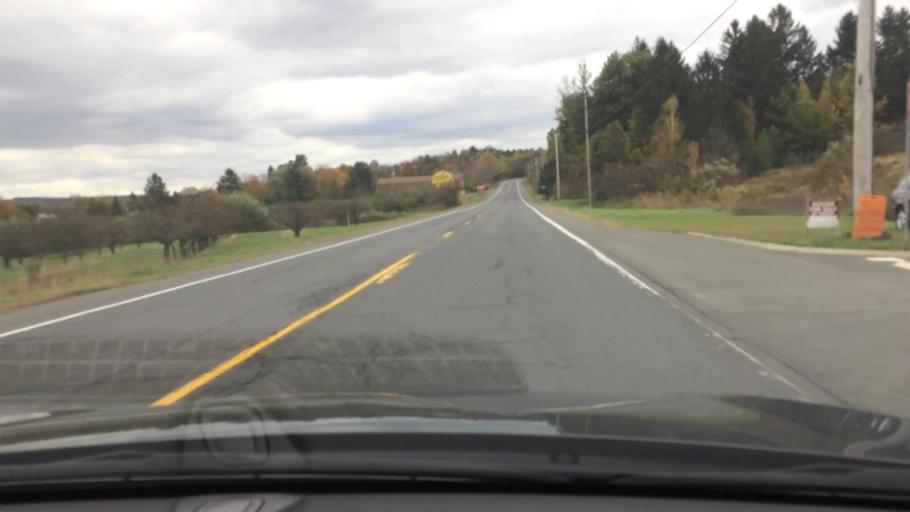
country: US
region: New York
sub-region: Columbia County
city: Oakdale
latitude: 42.1424
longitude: -73.7400
